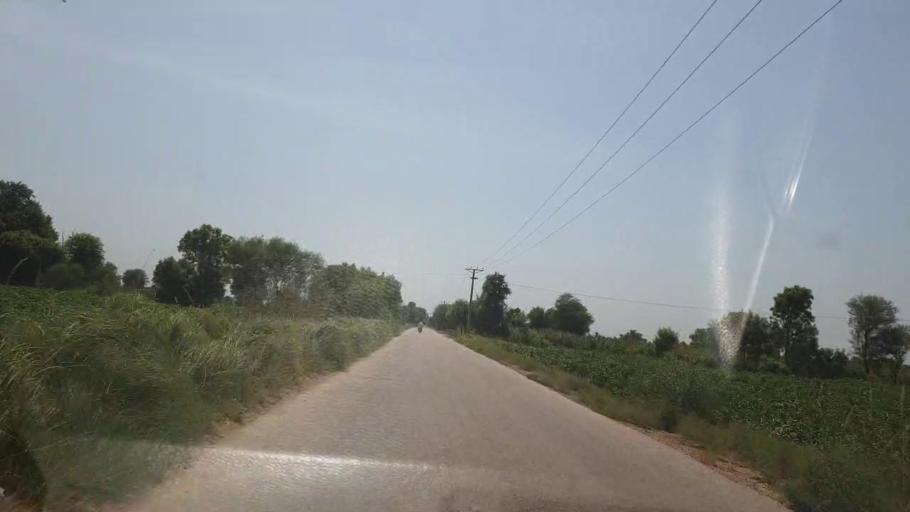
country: PK
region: Sindh
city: Bozdar
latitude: 27.0615
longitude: 68.5777
